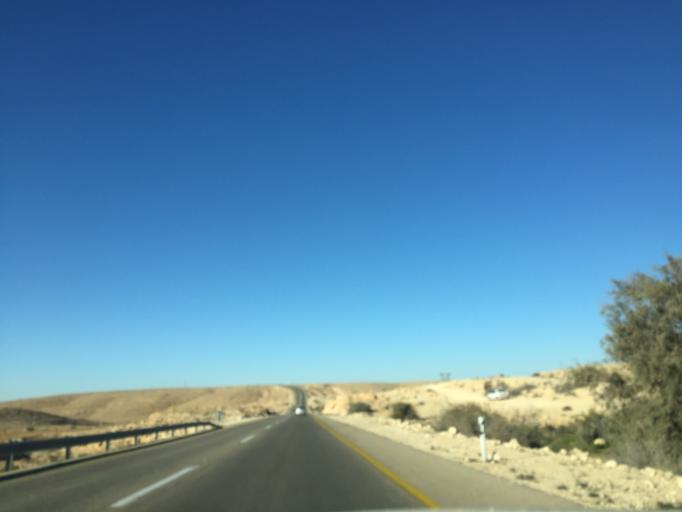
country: IL
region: Southern District
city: Mitzpe Ramon
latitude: 30.6694
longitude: 34.8046
